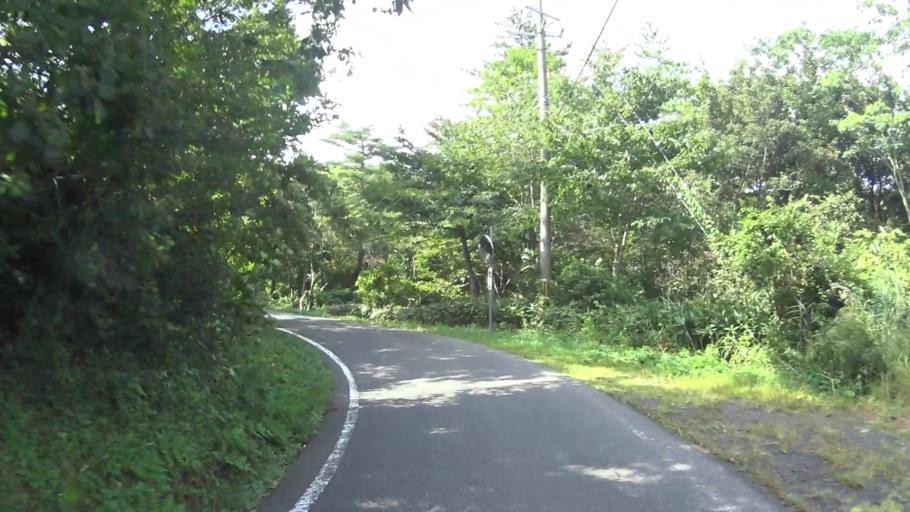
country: JP
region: Kyoto
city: Miyazu
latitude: 35.6482
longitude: 135.1802
